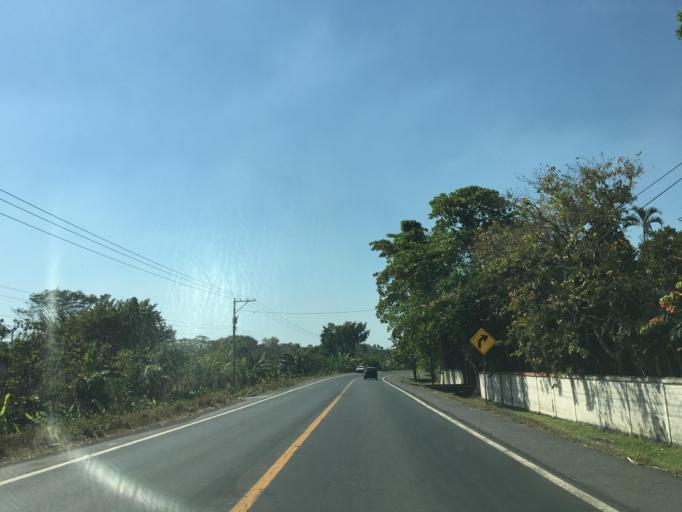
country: GT
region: Escuintla
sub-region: Municipio de Masagua
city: Masagua
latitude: 14.1589
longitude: -90.8802
